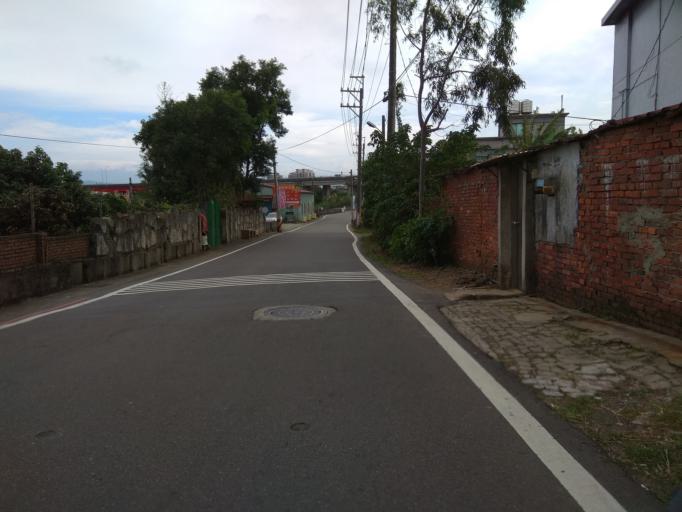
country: TW
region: Taiwan
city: Daxi
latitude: 24.9303
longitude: 121.2052
